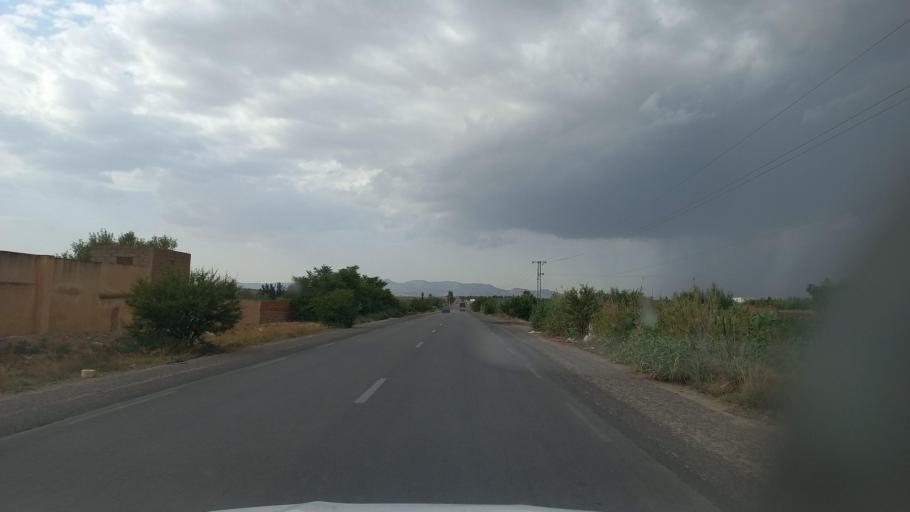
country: TN
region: Al Qasrayn
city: Sbiba
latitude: 35.3031
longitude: 9.0877
